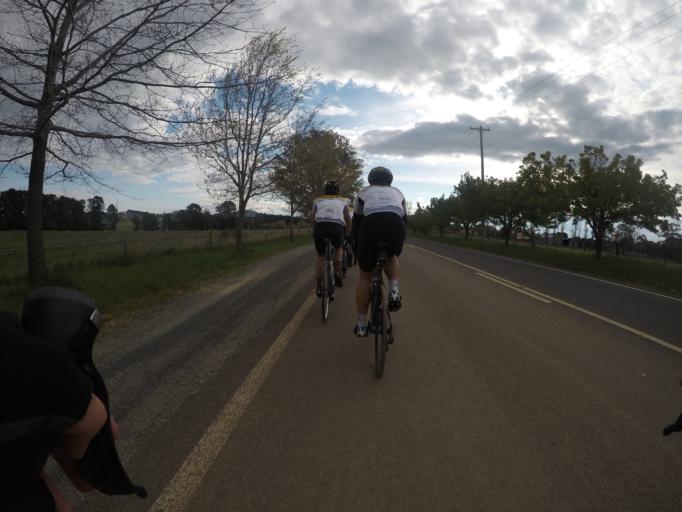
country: AU
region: New South Wales
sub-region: Orange Municipality
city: Orange
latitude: -33.2858
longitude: 149.0563
